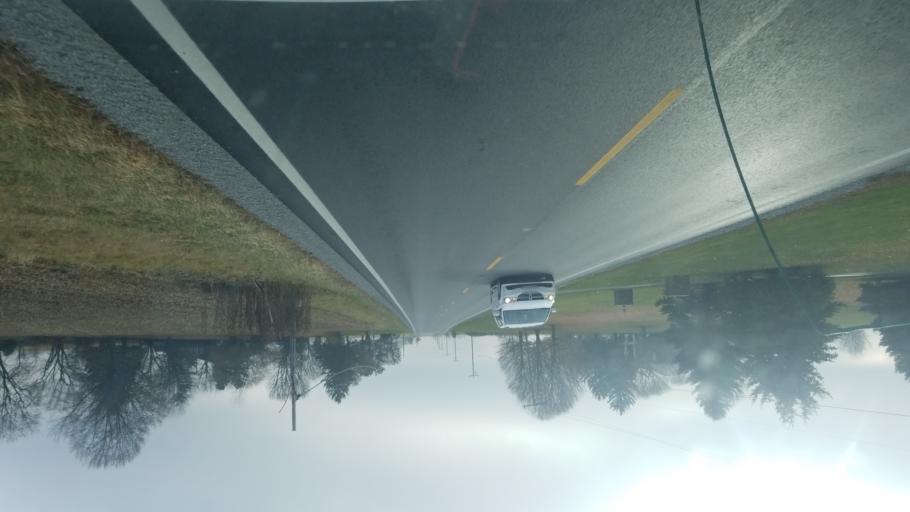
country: US
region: Ohio
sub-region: Hardin County
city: Kenton
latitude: 40.6619
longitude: -83.5642
